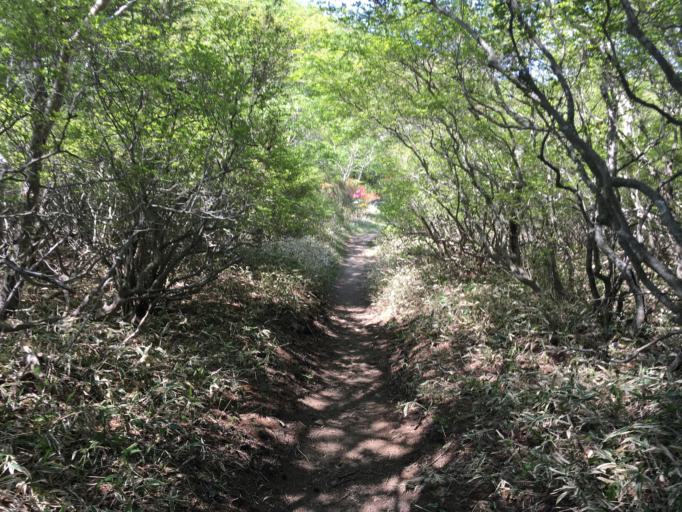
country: JP
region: Iwate
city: Ofunato
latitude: 39.1877
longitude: 141.7311
